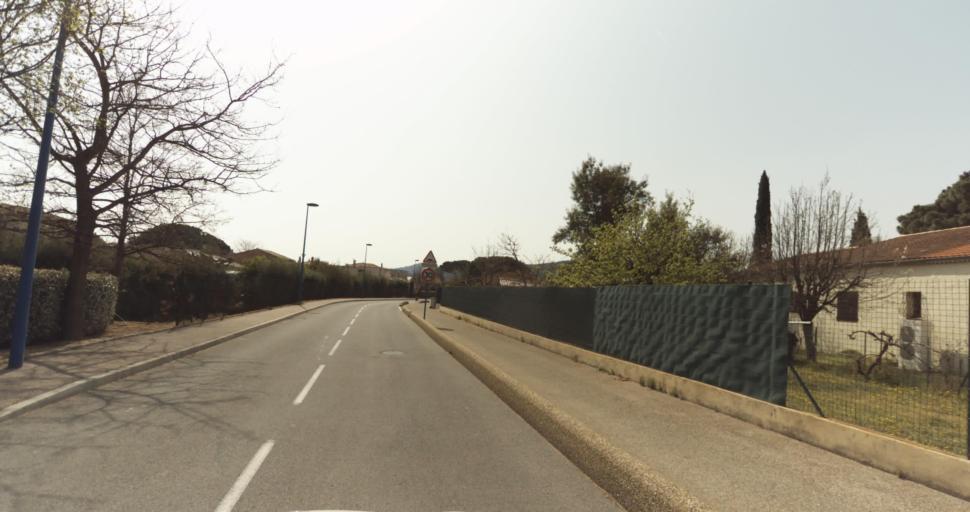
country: FR
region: Provence-Alpes-Cote d'Azur
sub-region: Departement du Var
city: Bormes-les-Mimosas
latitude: 43.1361
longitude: 6.3464
